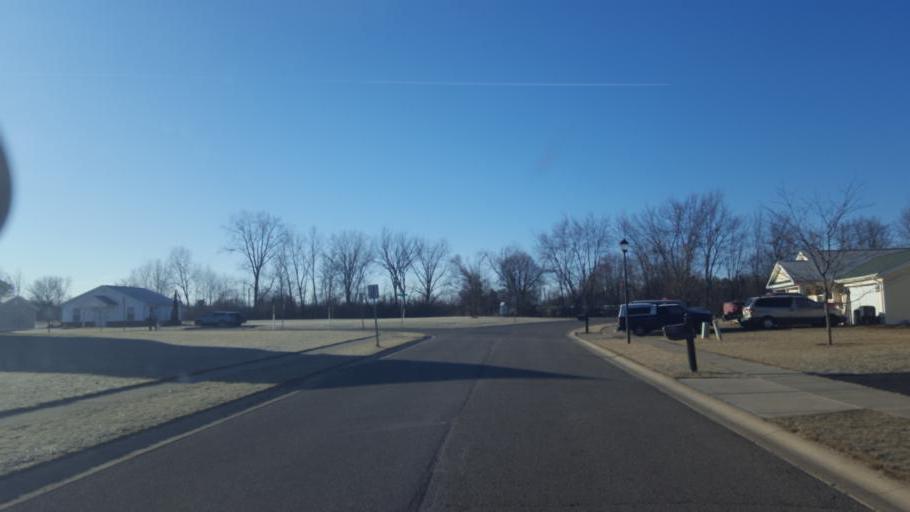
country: US
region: Ohio
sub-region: Morrow County
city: Mount Gilead
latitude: 40.5540
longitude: -82.8482
